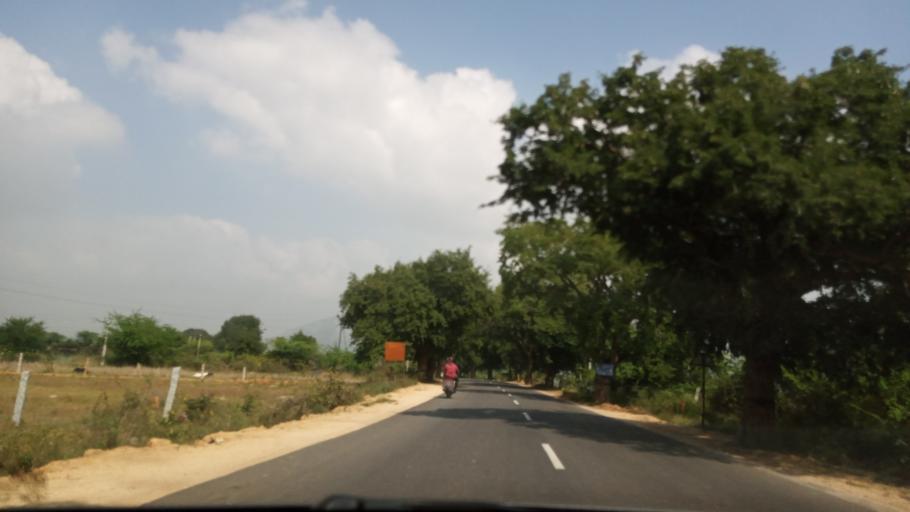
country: IN
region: Andhra Pradesh
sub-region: Chittoor
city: Madanapalle
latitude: 13.6153
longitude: 78.5426
